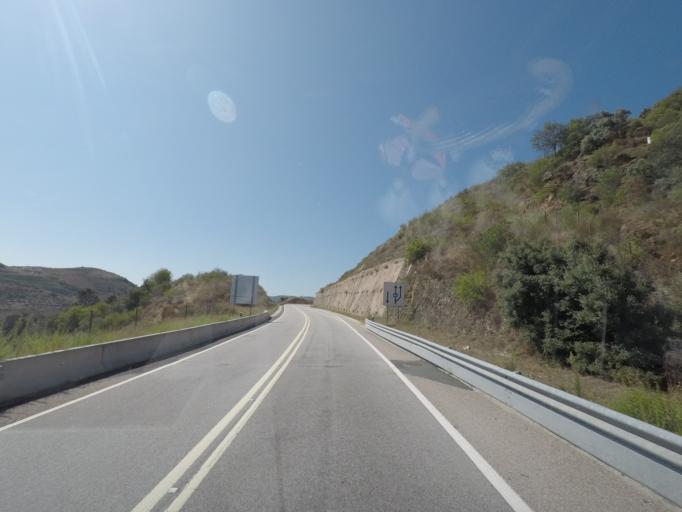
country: PT
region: Braganca
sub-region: Alfandega da Fe
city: Alfandega da Fe
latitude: 41.2859
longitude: -6.8772
